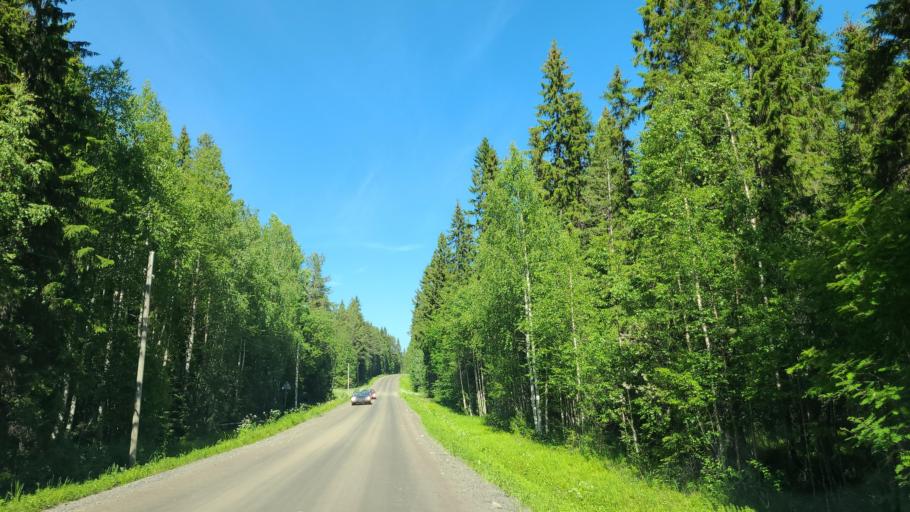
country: SE
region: Vaesterbotten
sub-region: Bjurholms Kommun
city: Bjurholm
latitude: 63.6985
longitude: 18.8967
